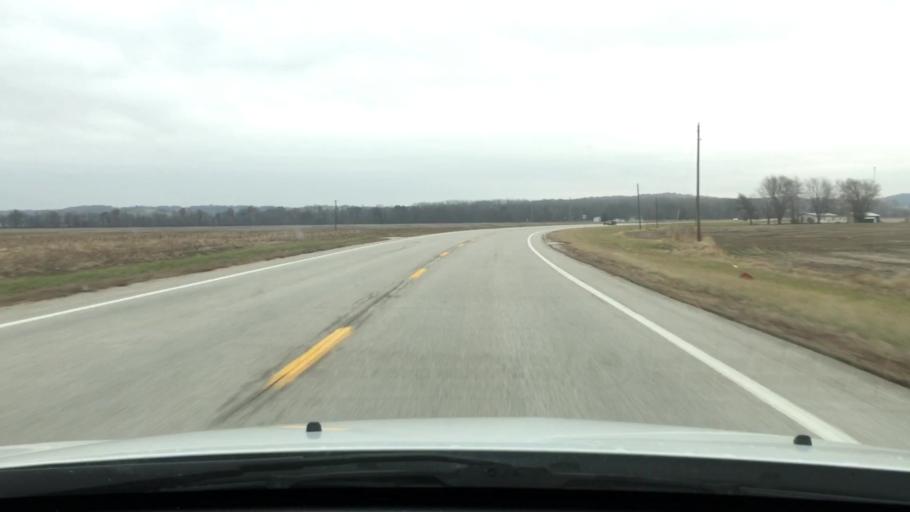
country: US
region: Missouri
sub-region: Pike County
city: Louisiana
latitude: 39.4974
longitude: -91.0016
